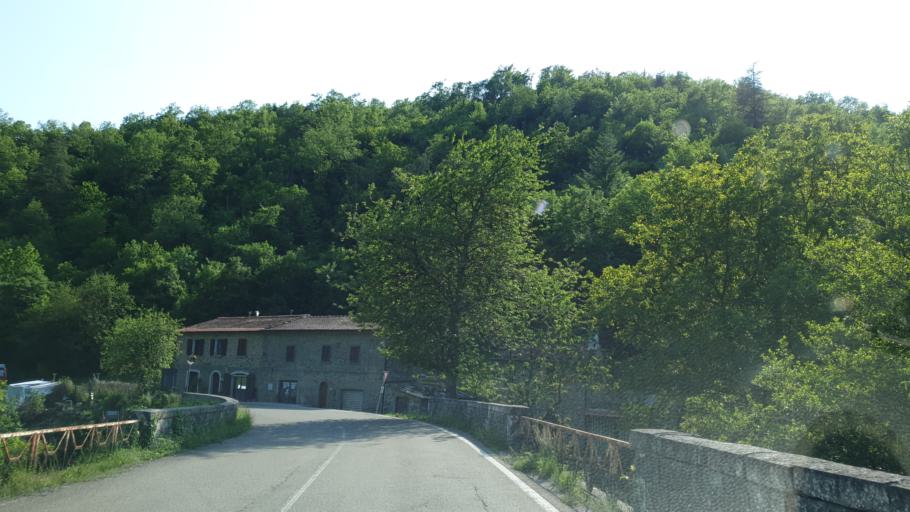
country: IT
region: Tuscany
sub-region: Province of Arezzo
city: Soci
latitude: 43.7674
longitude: 11.8365
